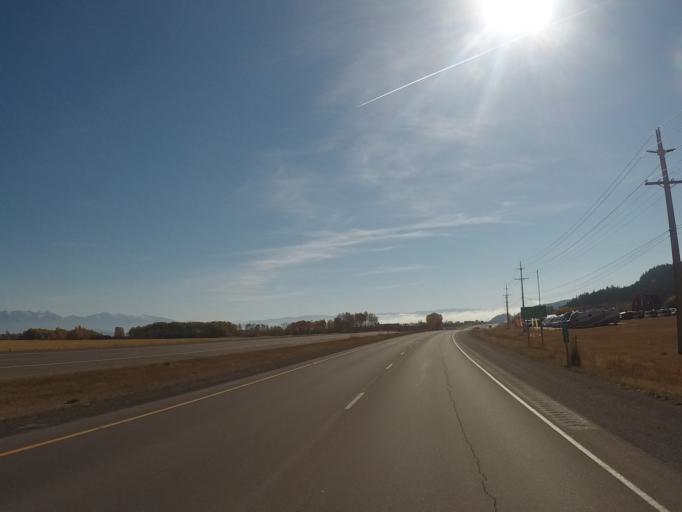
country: US
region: Montana
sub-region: Flathead County
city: Somers
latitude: 48.1301
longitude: -114.2665
